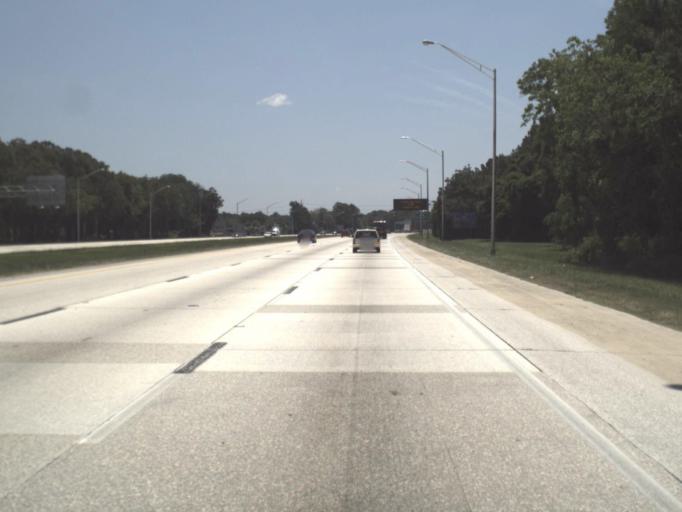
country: US
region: Florida
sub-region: Duval County
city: Jacksonville
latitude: 30.2397
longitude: -81.5845
